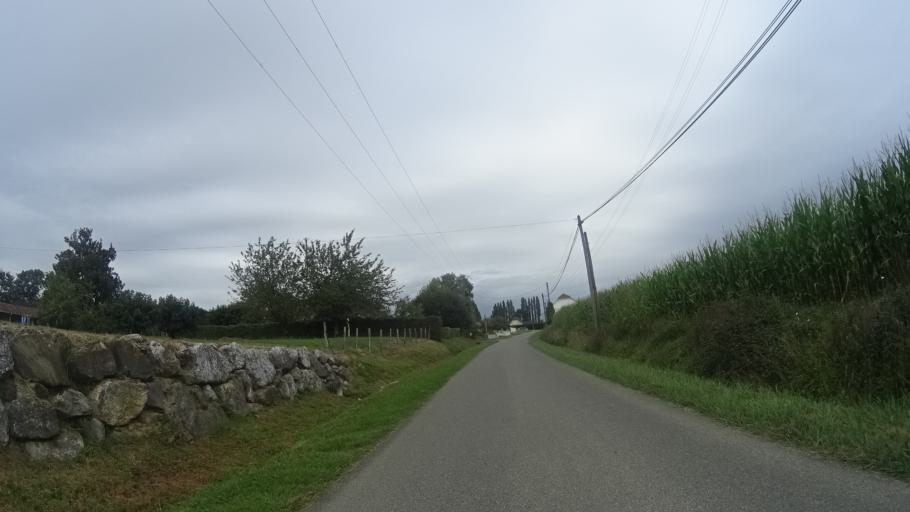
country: FR
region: Aquitaine
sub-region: Departement des Pyrenees-Atlantiques
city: Orthez
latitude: 43.4806
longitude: -0.7245
